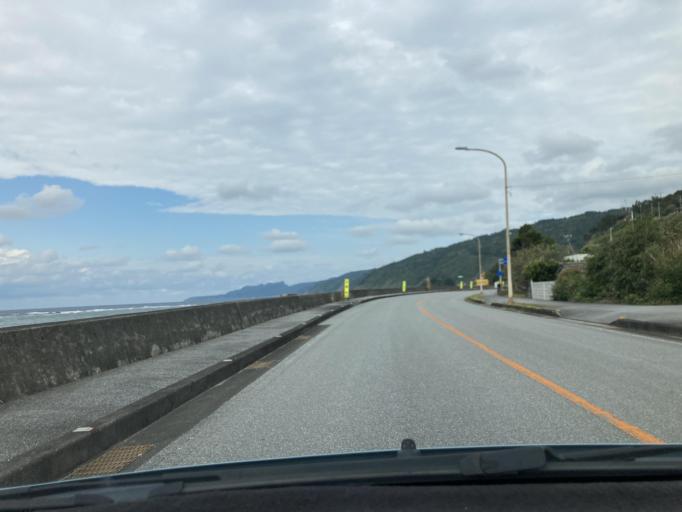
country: JP
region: Okinawa
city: Nago
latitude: 26.7813
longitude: 128.2140
